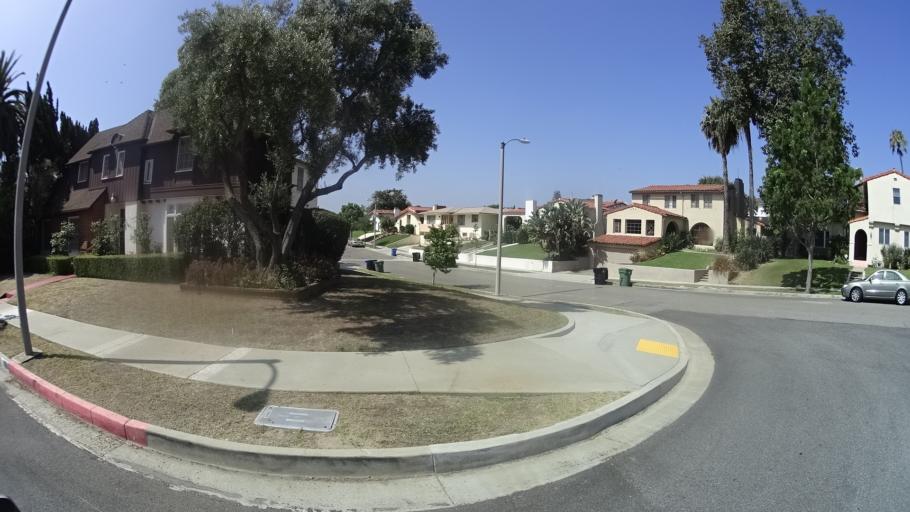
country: US
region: California
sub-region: Los Angeles County
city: View Park-Windsor Hills
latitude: 33.9991
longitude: -118.3420
